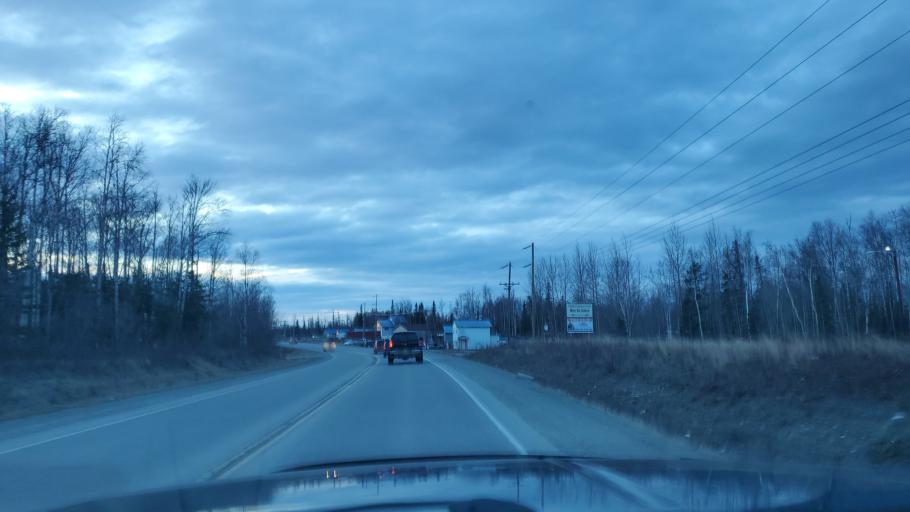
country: US
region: Alaska
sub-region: Matanuska-Susitna Borough
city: Tanaina
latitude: 61.5935
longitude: -149.3883
